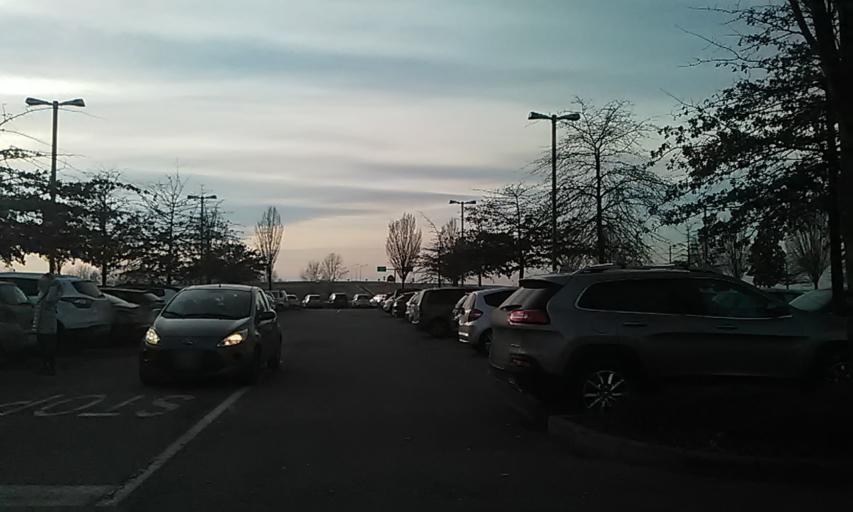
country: IT
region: Piedmont
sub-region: Provincia di Novara
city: Vicolungo
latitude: 45.4670
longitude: 8.4592
